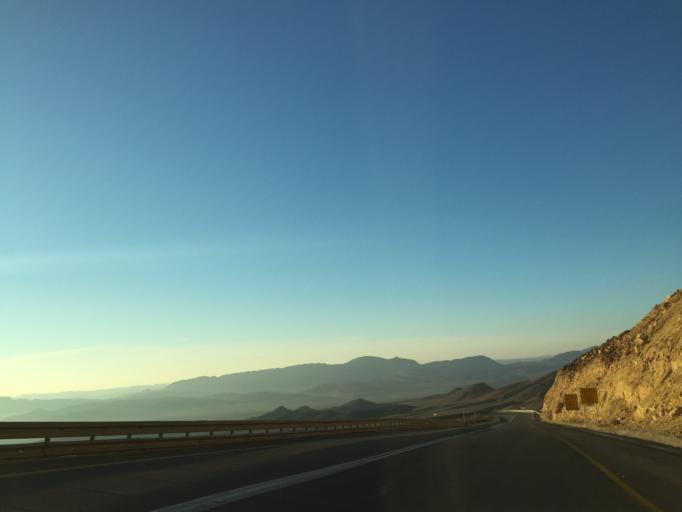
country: IL
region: Southern District
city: Mitzpe Ramon
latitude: 30.6234
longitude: 34.8179
